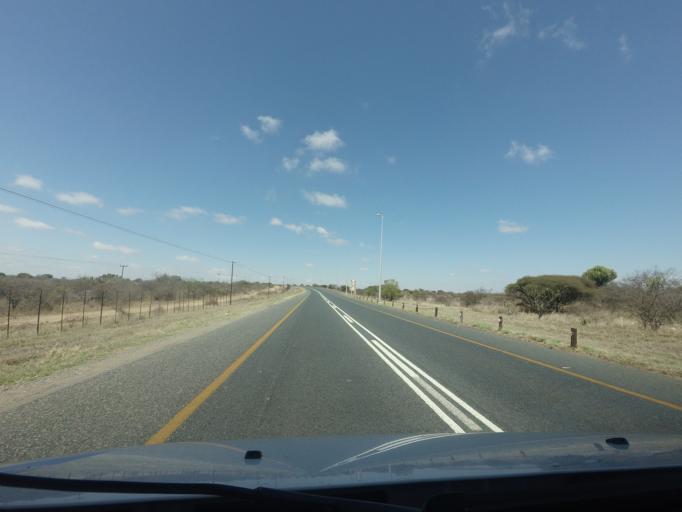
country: ZA
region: Limpopo
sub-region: Vhembe District Municipality
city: Louis Trichardt
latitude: -23.3707
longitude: 29.7719
